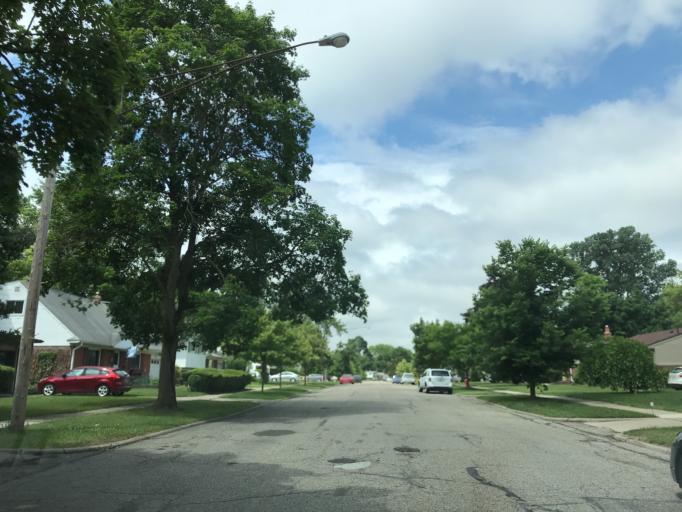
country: US
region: Michigan
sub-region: Washtenaw County
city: Ann Arbor
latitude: 42.2389
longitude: -83.7031
